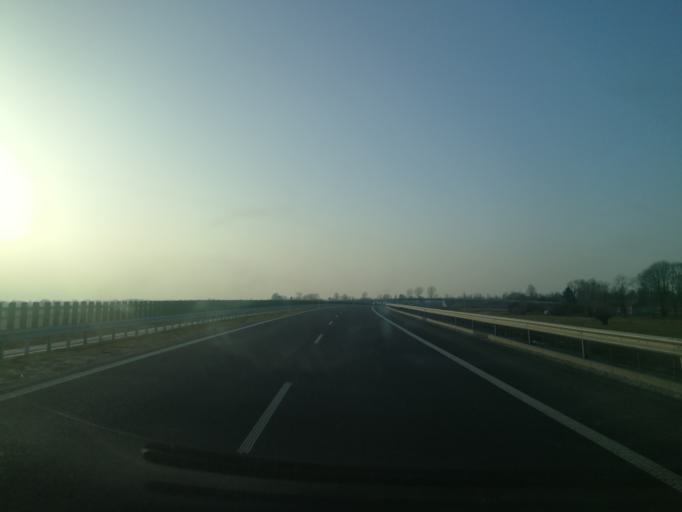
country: PL
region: Pomeranian Voivodeship
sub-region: Powiat nowodworski
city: Nowy Dwor Gdanski
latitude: 54.1741
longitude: 19.1977
